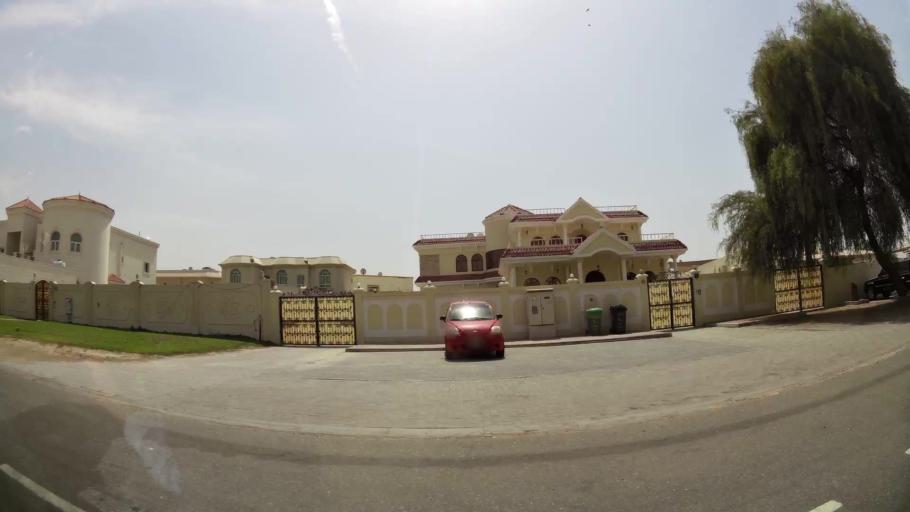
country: AE
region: Ash Shariqah
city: Sharjah
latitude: 25.2395
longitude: 55.4369
